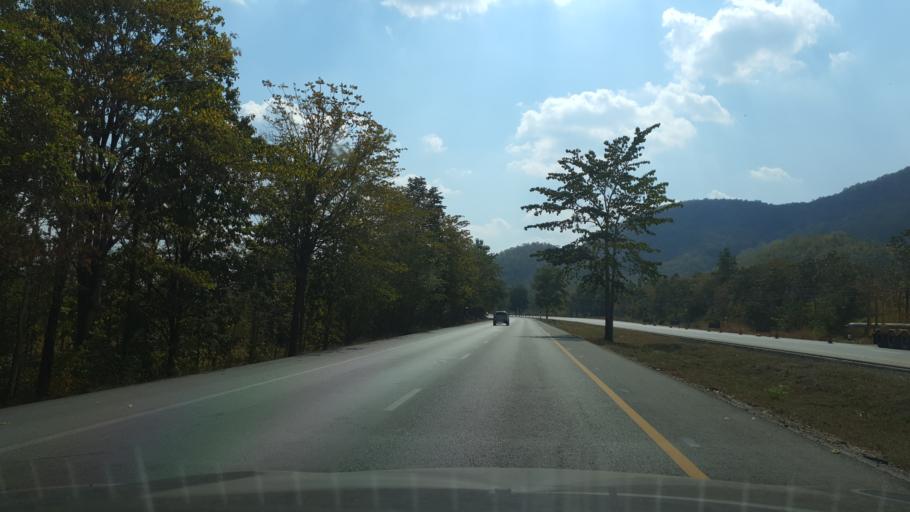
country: TH
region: Lampang
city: Mae Phrik
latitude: 17.3455
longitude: 99.1496
